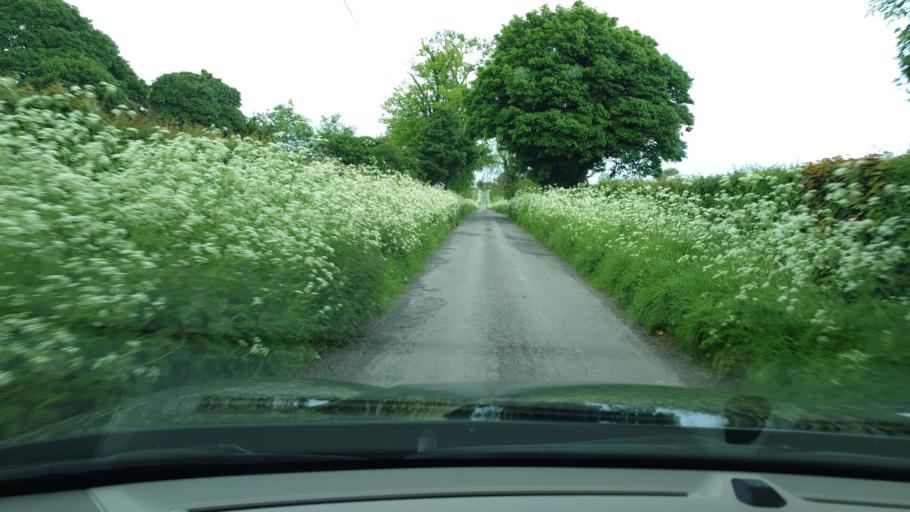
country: IE
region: Leinster
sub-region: An Mhi
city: Ratoath
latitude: 53.5269
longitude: -6.4624
